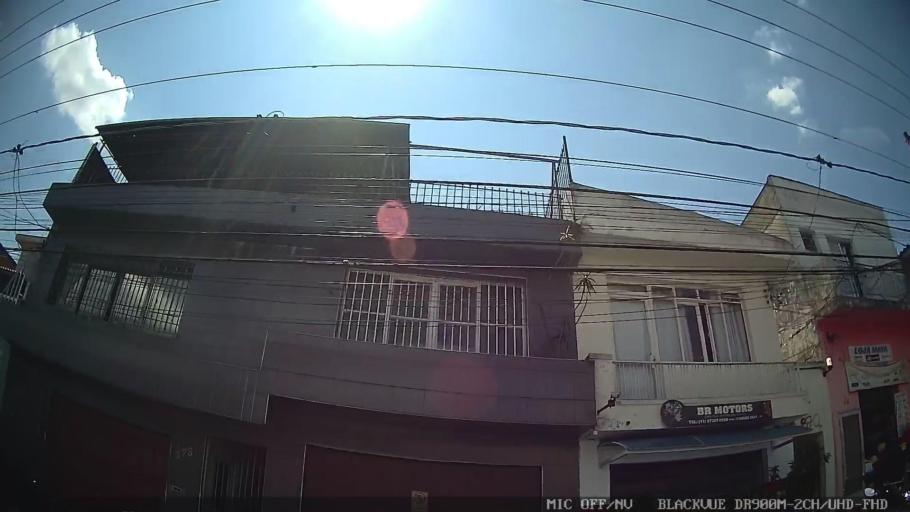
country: BR
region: Sao Paulo
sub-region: Guarulhos
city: Guarulhos
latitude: -23.5216
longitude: -46.4901
